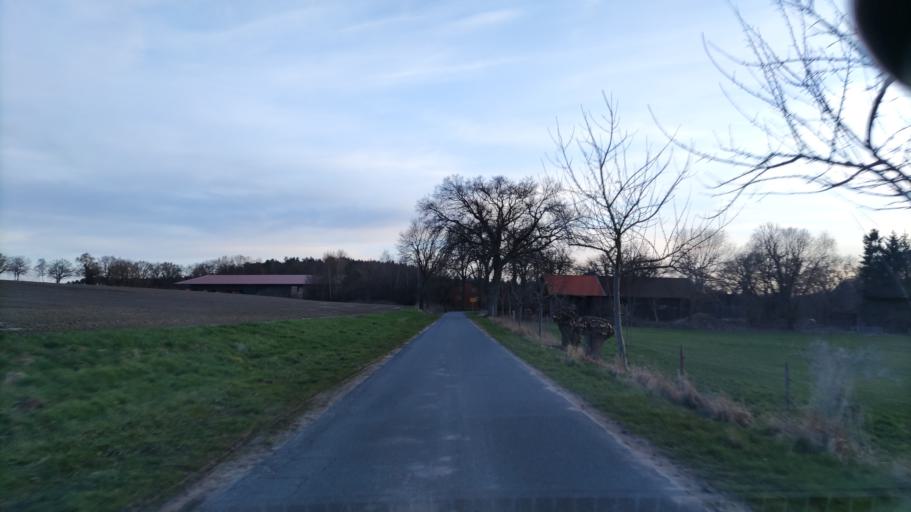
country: DE
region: Lower Saxony
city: Dahlenburg
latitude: 53.2096
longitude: 10.7019
